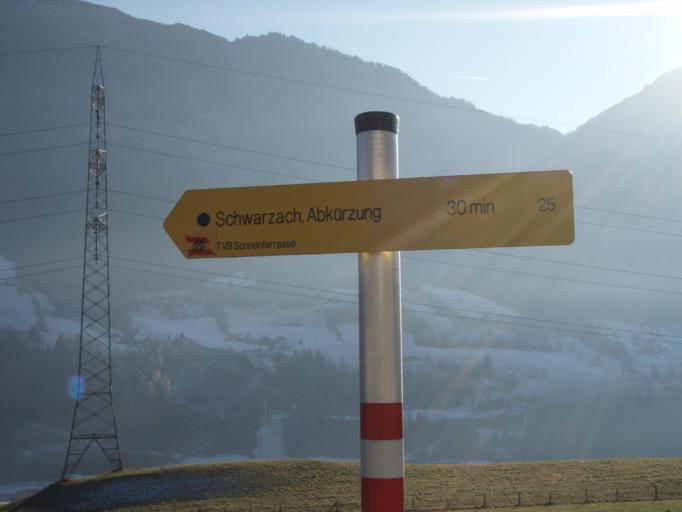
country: AT
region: Salzburg
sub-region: Politischer Bezirk Sankt Johann im Pongau
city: Schwarzach im Pongau
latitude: 47.3268
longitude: 13.1526
